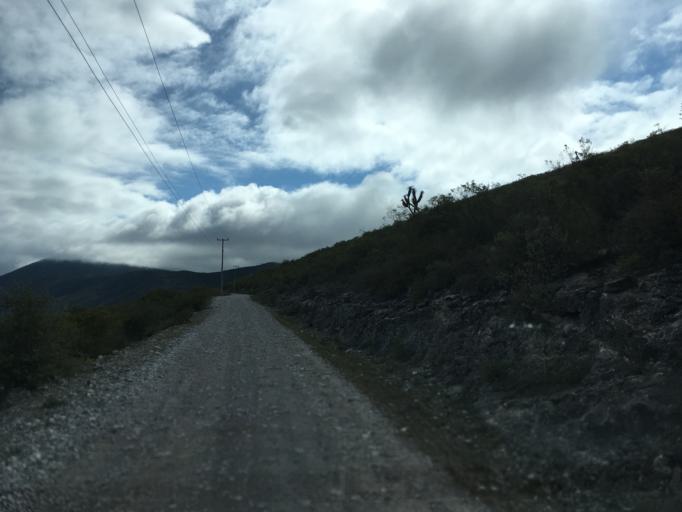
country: MX
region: Hidalgo
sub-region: Metztitlan
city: Fontezuelas
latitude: 20.6412
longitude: -98.8520
